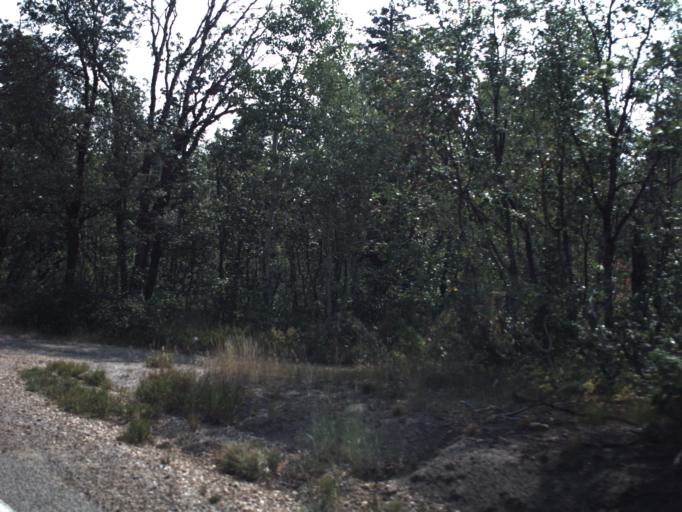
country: US
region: Utah
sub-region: Summit County
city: Summit Park
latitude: 40.8365
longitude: -111.6427
